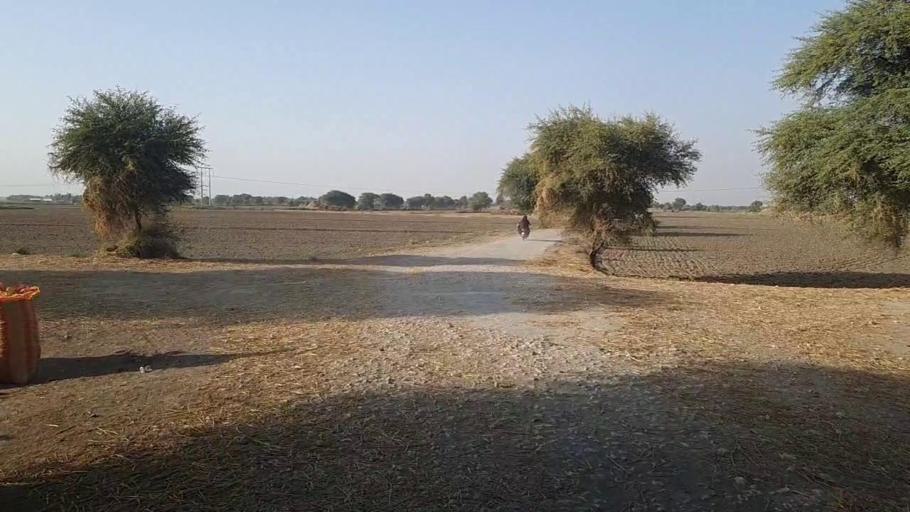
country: PK
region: Sindh
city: Kashmor
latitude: 28.4088
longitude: 69.4125
